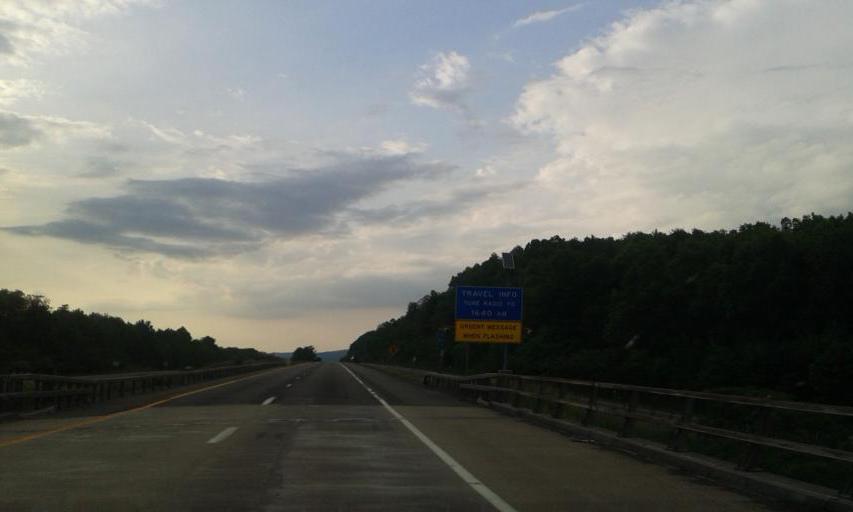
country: US
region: Pennsylvania
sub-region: Susquehanna County
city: Hallstead
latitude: 42.0427
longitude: -75.7925
